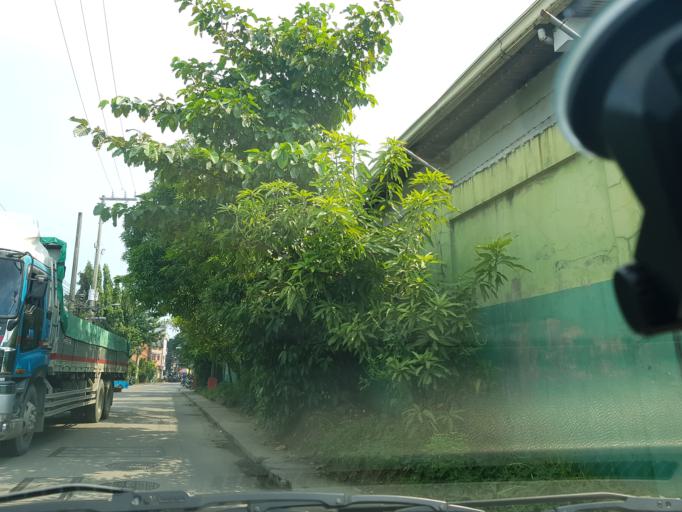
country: PH
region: Calabarzon
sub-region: Province of Rizal
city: Pateros
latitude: 14.5449
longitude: 121.0783
